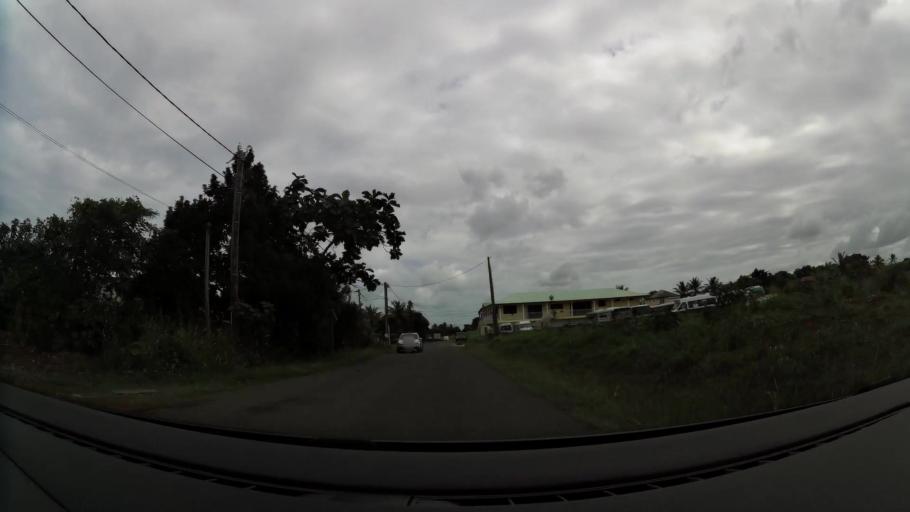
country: GP
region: Guadeloupe
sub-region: Guadeloupe
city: Sainte-Rose
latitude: 16.3234
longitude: -61.6970
